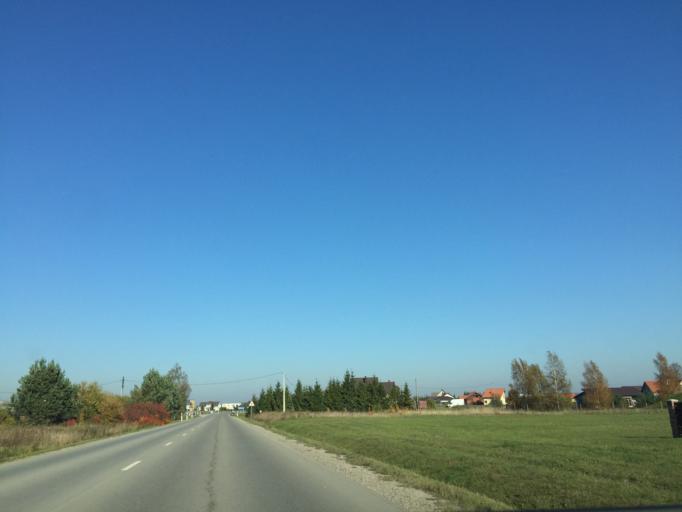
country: LT
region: Klaipedos apskritis
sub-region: Klaipeda
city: Klaipeda
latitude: 55.7534
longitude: 21.1926
